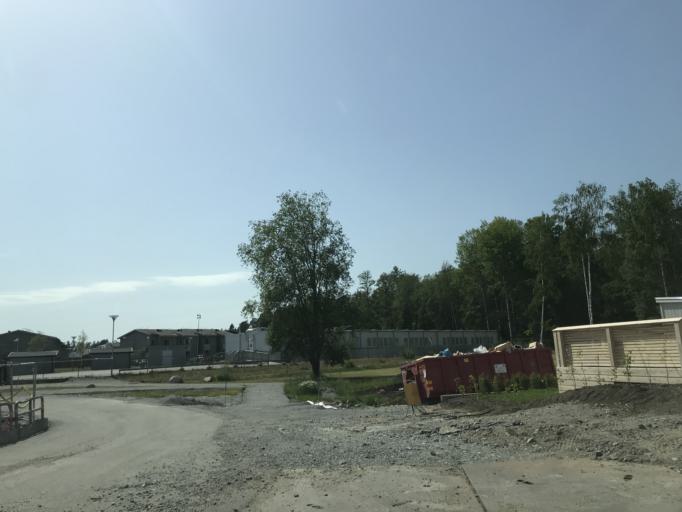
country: SE
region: Stockholm
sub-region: Solna Kommun
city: Rasunda
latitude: 59.3868
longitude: 17.9851
